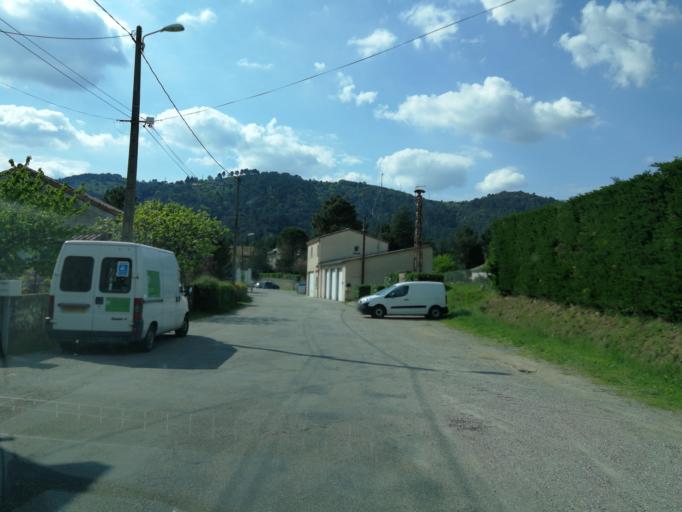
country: FR
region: Rhone-Alpes
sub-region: Departement de l'Ardeche
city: Saint-Sauveur-de-Montagut
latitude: 44.8052
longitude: 4.6204
